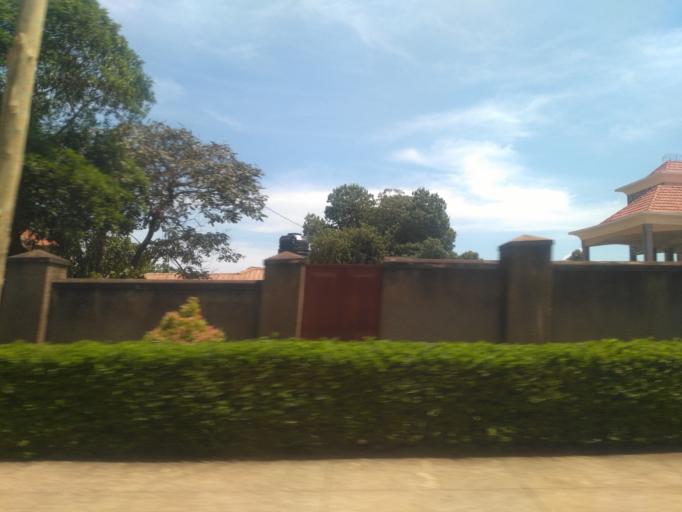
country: UG
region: Central Region
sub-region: Wakiso District
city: Entebbe
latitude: 0.0475
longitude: 32.4647
